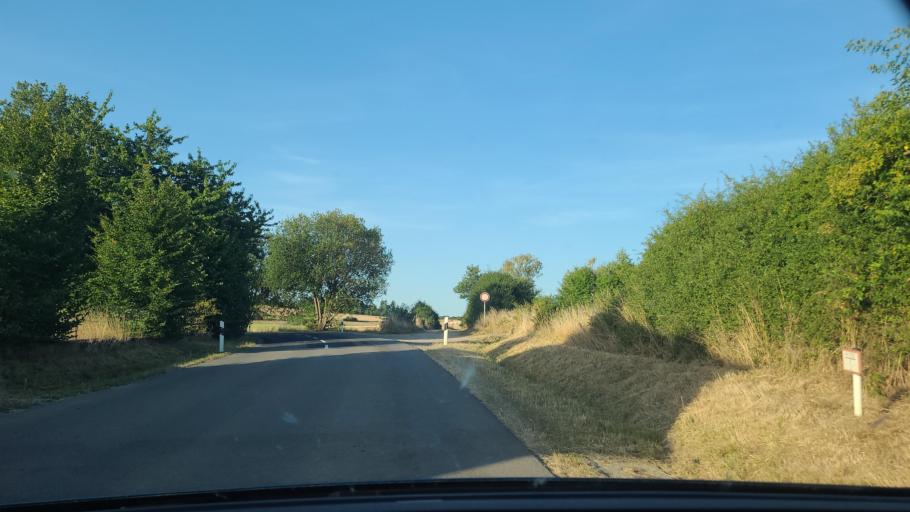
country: LU
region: Luxembourg
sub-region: Canton de Capellen
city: Dippach
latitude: 49.6123
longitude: 5.9900
